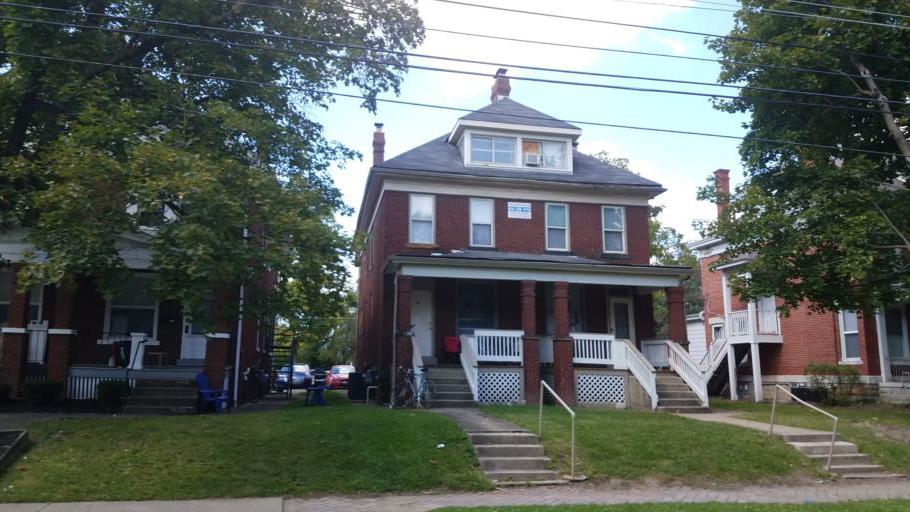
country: US
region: Ohio
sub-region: Franklin County
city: Columbus
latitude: 40.0010
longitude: -82.9986
